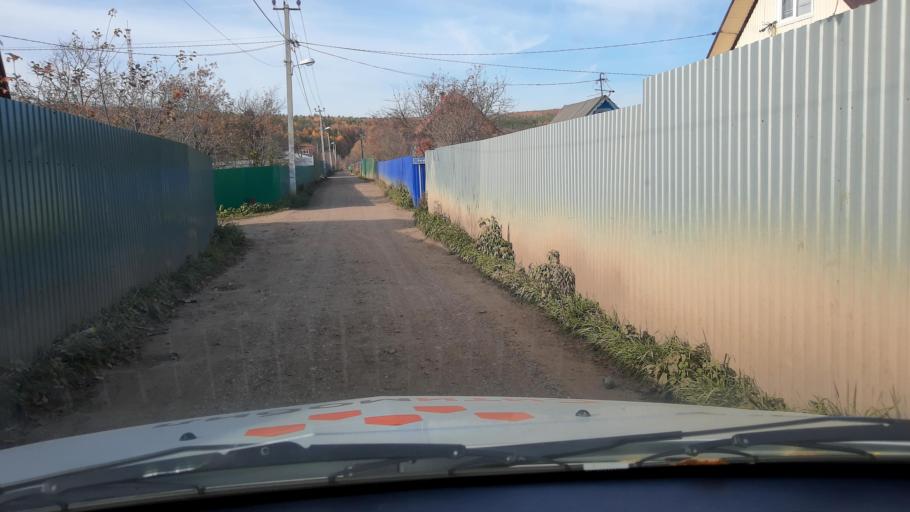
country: RU
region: Bashkortostan
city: Ufa
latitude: 54.8097
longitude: 56.1551
